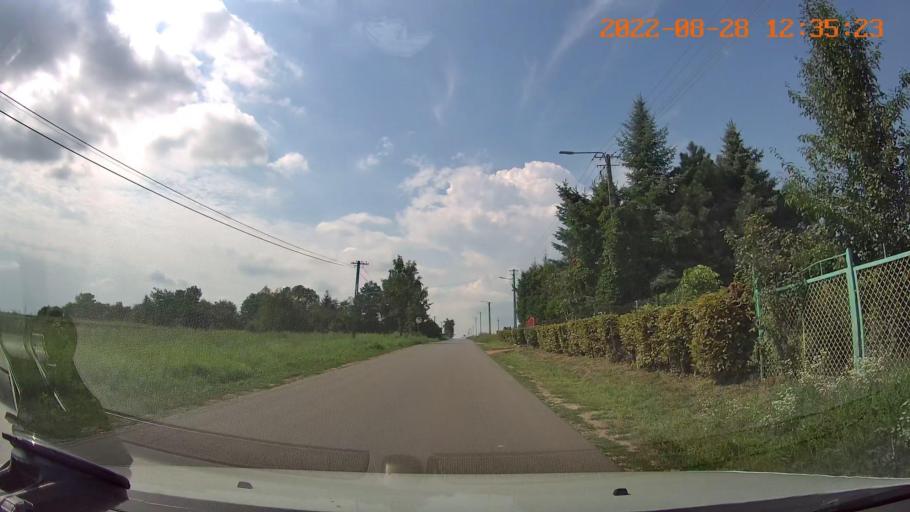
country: PL
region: Swietokrzyskie
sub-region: Powiat kazimierski
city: Skalbmierz
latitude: 50.3751
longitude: 20.4214
